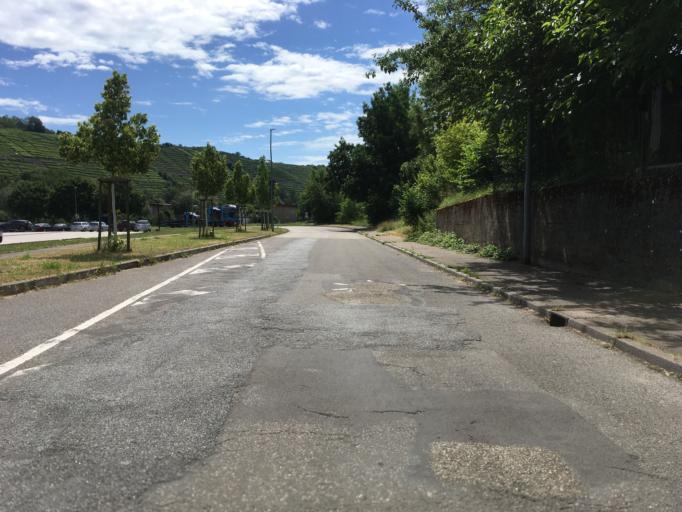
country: DE
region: Baden-Wuerttemberg
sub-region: Regierungsbezirk Stuttgart
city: Besigheim
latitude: 48.9932
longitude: 9.1432
